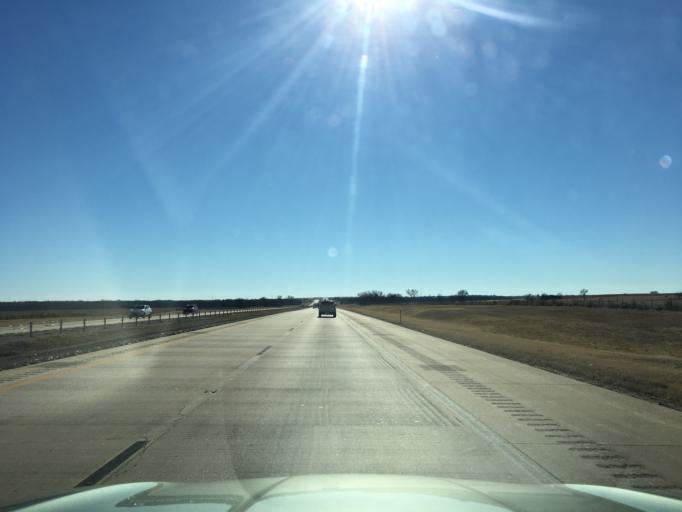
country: US
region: Oklahoma
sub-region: Noble County
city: Perry
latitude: 36.4473
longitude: -97.3271
